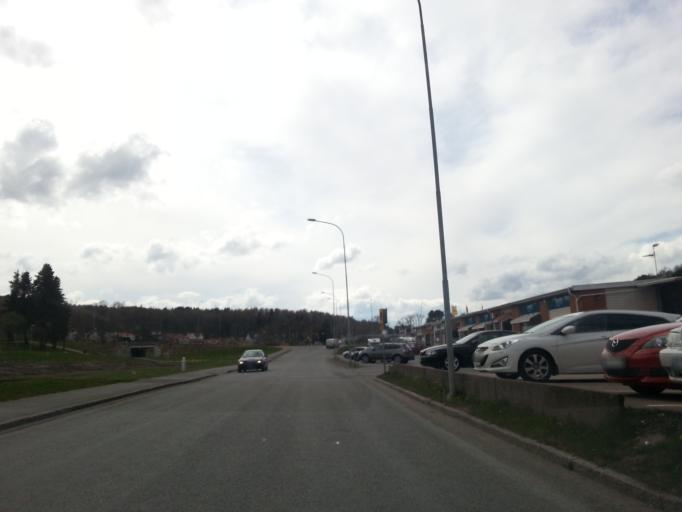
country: SE
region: Vaestra Goetaland
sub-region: Kungalvs Kommun
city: Kungalv
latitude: 57.8720
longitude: 11.9522
